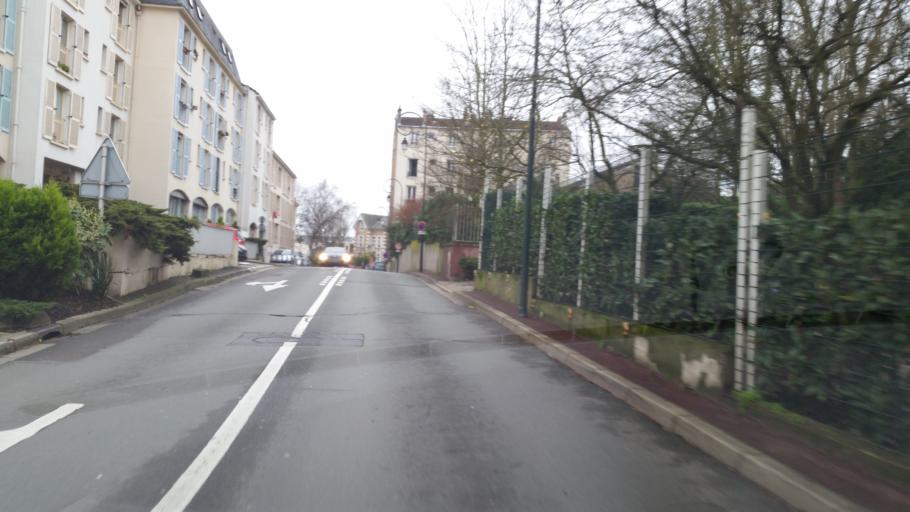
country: FR
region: Ile-de-France
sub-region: Departement des Hauts-de-Seine
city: Garches
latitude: 48.8456
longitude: 2.1874
